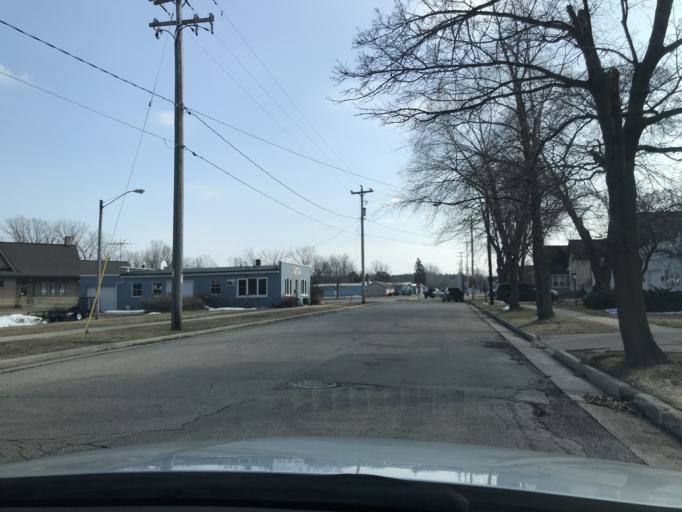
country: US
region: Wisconsin
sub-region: Marinette County
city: Marinette
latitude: 45.0985
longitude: -87.6389
